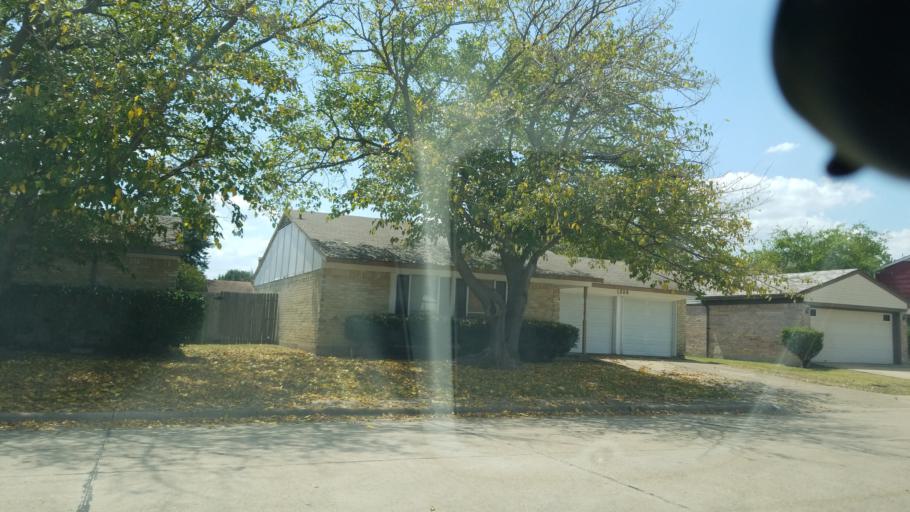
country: US
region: Texas
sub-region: Dallas County
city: Grand Prairie
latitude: 32.6999
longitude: -96.9880
